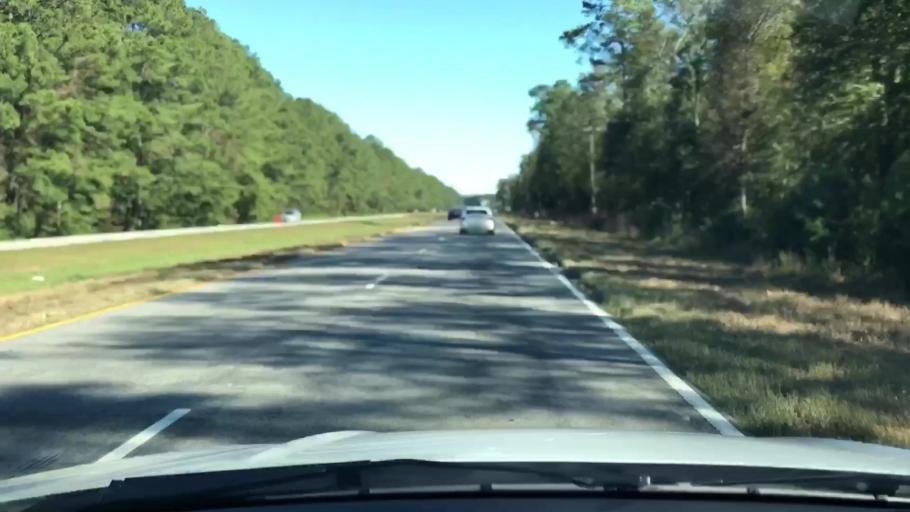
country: US
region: South Carolina
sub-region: Charleston County
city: Ravenel
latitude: 32.7816
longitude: -80.1932
